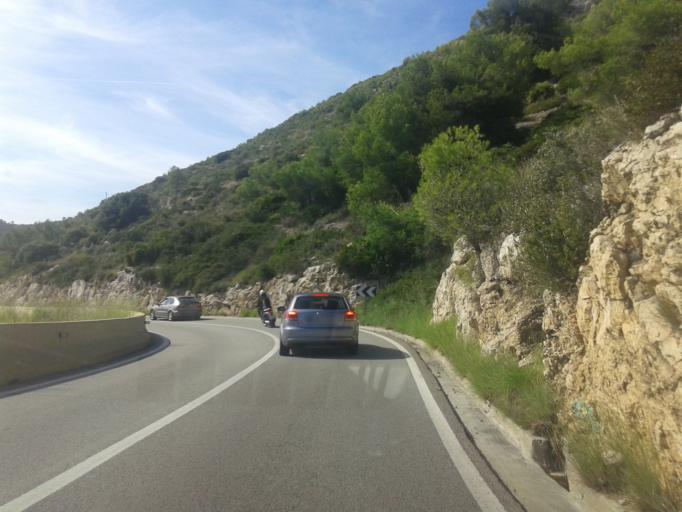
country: ES
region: Catalonia
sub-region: Provincia de Barcelona
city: Sitges
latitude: 41.2458
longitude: 1.8765
